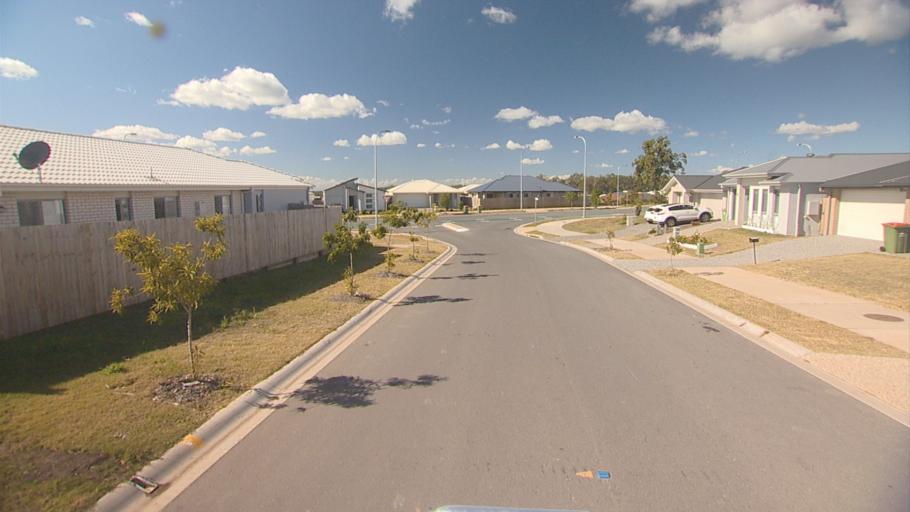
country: AU
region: Queensland
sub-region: Logan
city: Logan Reserve
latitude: -27.7153
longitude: 153.0832
